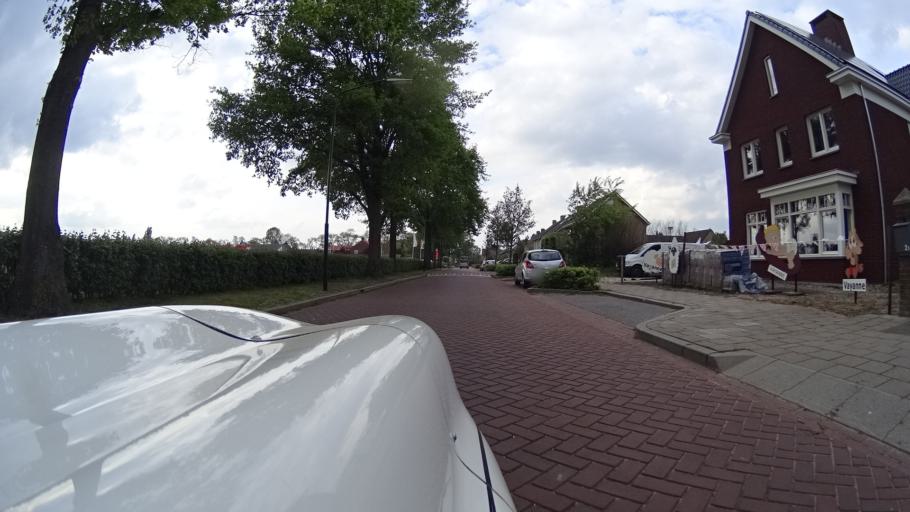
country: NL
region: North Brabant
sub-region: Gemeente Uden
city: Odiliapeel
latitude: 51.6072
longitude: 5.7344
